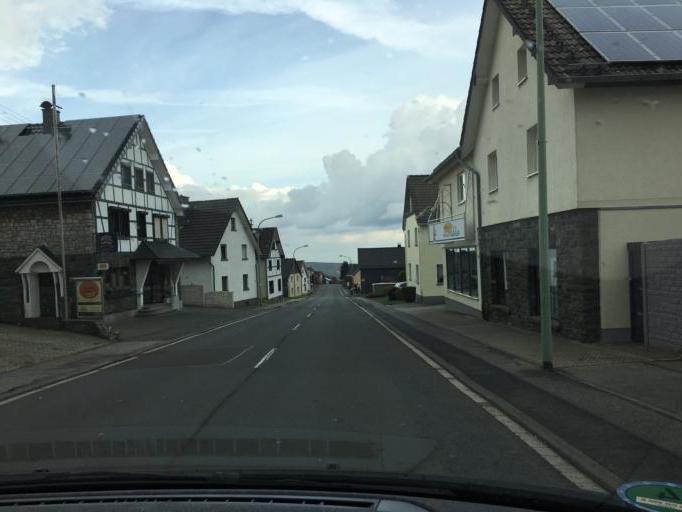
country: DE
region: North Rhine-Westphalia
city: Heimbach
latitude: 50.6602
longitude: 6.4110
